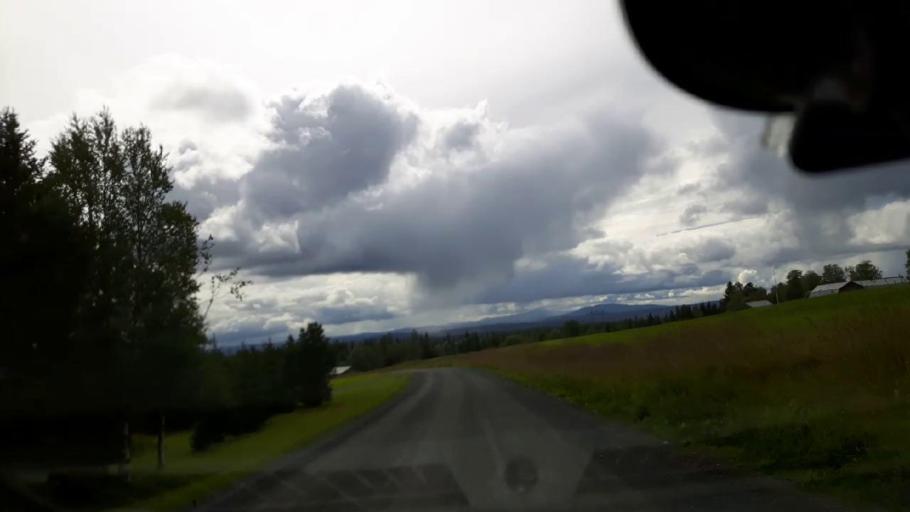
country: SE
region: Jaemtland
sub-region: Krokoms Kommun
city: Valla
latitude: 63.3529
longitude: 13.8316
